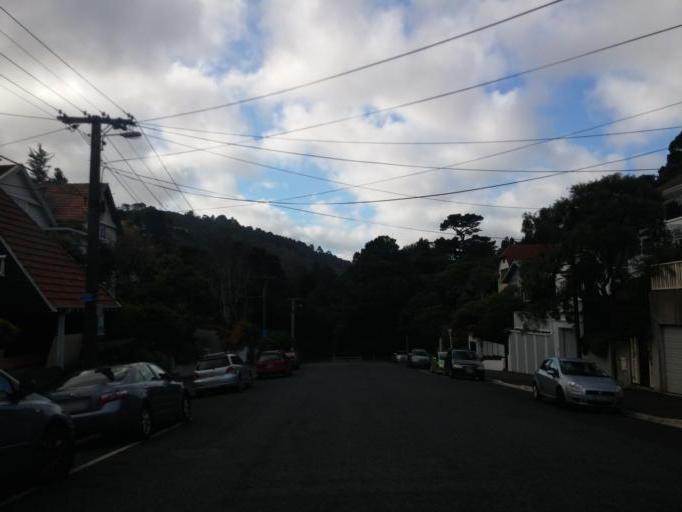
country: NZ
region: Wellington
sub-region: Wellington City
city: Kelburn
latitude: -41.2856
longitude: 174.7643
